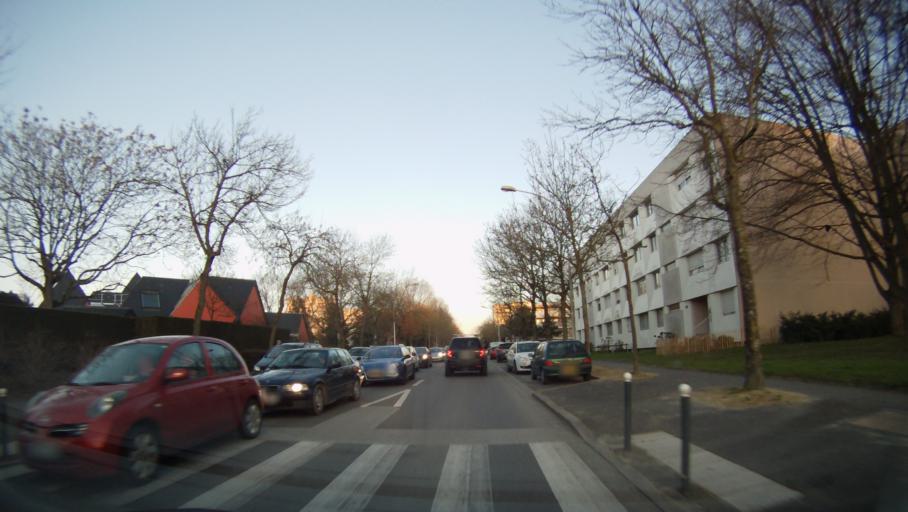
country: FR
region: Brittany
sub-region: Departement d'Ille-et-Vilaine
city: Rennes
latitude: 48.0866
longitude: -1.6730
